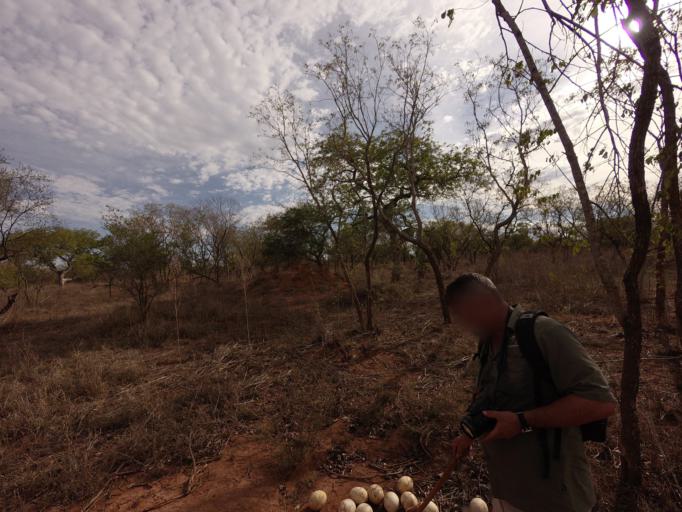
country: ZA
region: Limpopo
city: Thulamahashi
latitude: -24.5287
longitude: 31.1203
